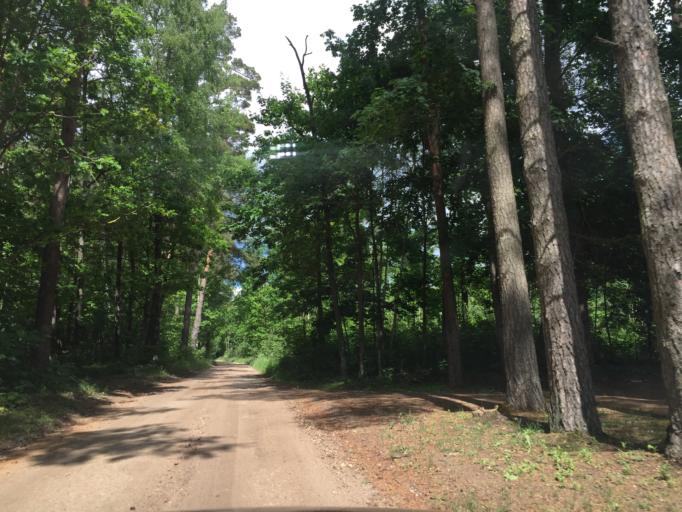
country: LV
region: Lecava
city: Iecava
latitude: 56.5621
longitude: 24.1106
